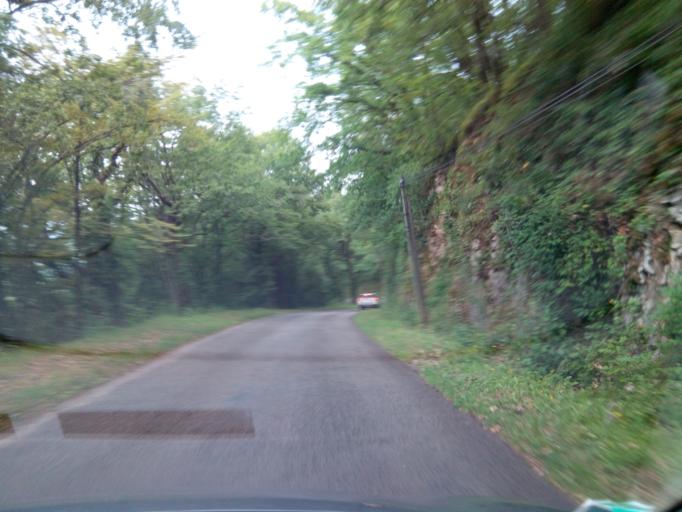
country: FR
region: Midi-Pyrenees
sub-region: Departement du Lot
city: Vayrac
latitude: 44.8958
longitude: 1.7534
